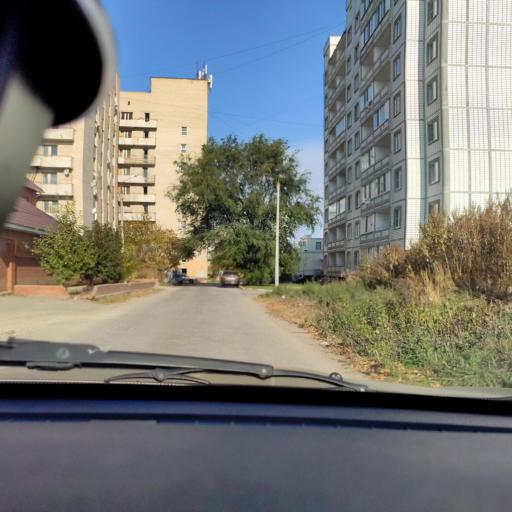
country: RU
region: Samara
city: Tol'yatti
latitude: 53.5383
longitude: 49.4061
